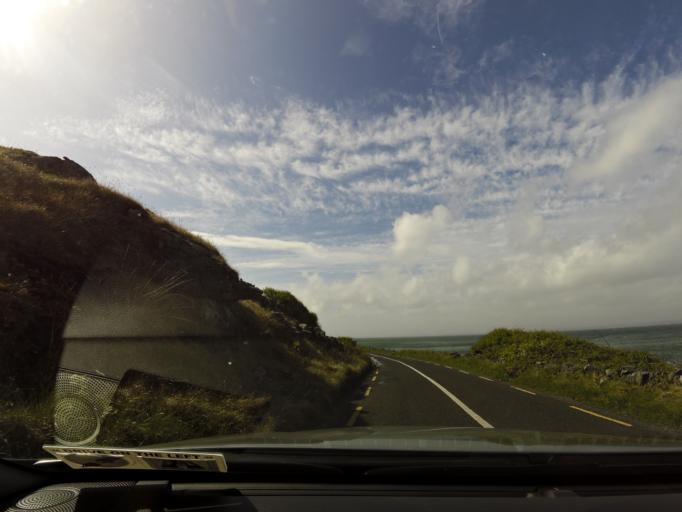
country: IE
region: Connaught
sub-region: County Galway
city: Bearna
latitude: 53.1484
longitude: -9.2394
